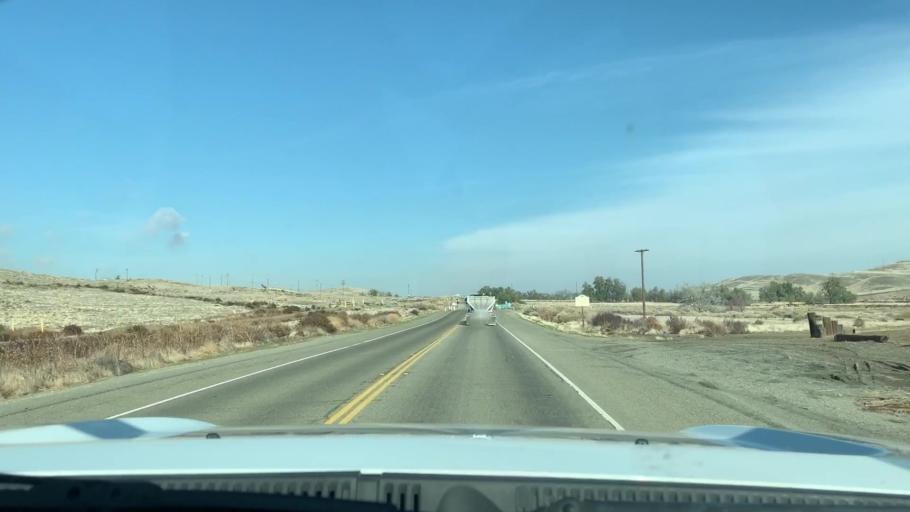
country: US
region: California
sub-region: Fresno County
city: Coalinga
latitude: 36.2428
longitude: -120.3150
